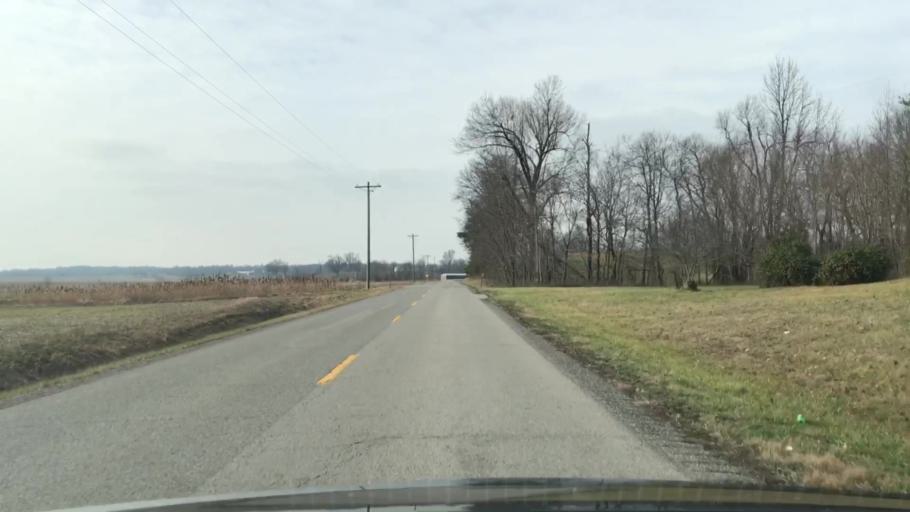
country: US
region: Kentucky
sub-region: McLean County
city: Calhoun
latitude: 37.5148
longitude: -87.4065
